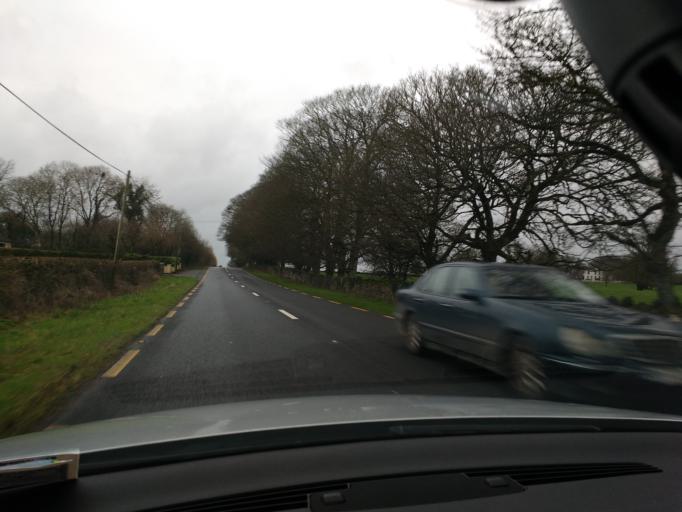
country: IE
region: Munster
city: Thurles
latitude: 52.6728
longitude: -7.7550
